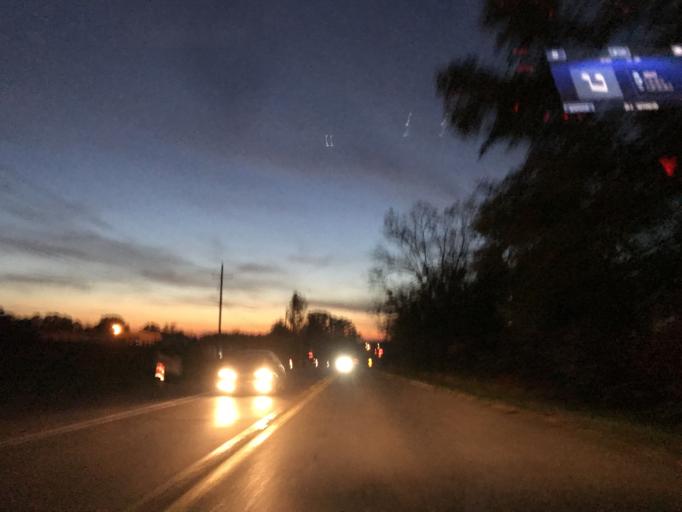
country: US
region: Michigan
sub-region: Oakland County
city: South Lyon
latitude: 42.4332
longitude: -83.6095
